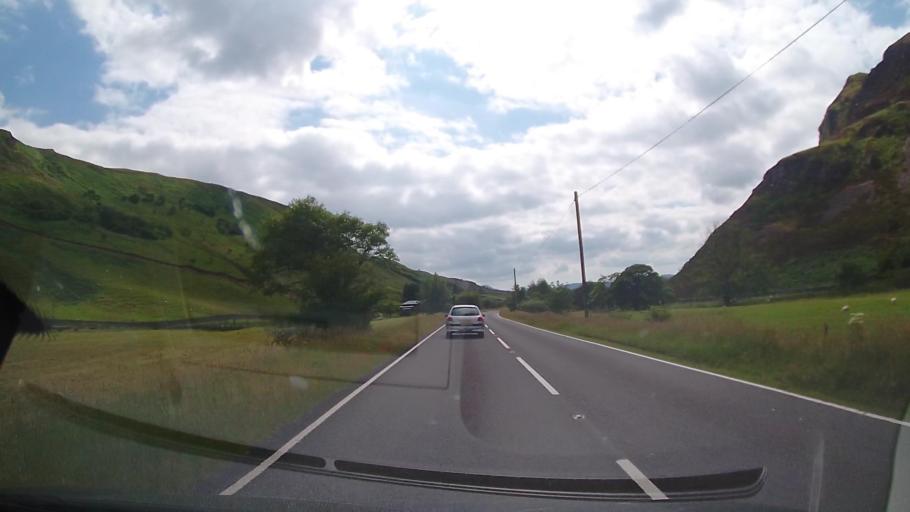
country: GB
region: Wales
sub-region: Gwynedd
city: Trawsfynydd
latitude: 52.9183
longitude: -3.8340
